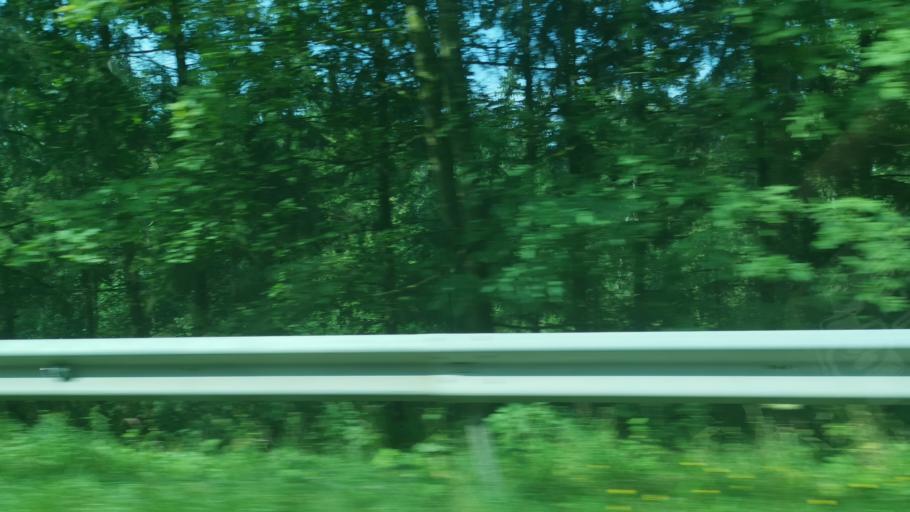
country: DE
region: Bavaria
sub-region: Upper Palatinate
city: Pemfling
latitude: 49.2792
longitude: 12.6253
